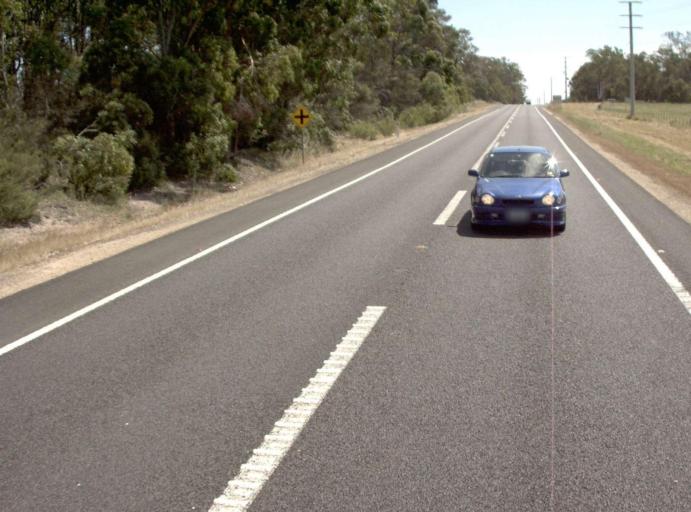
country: AU
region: Victoria
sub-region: East Gippsland
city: Bairnsdale
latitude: -37.9028
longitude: 147.3459
